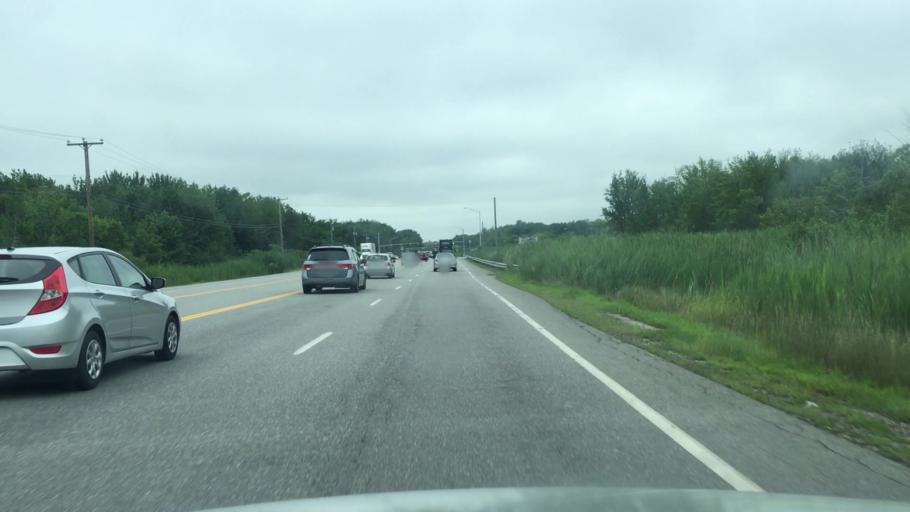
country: US
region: New Hampshire
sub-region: Rockingham County
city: Greenland
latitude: 43.0525
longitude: -70.8136
